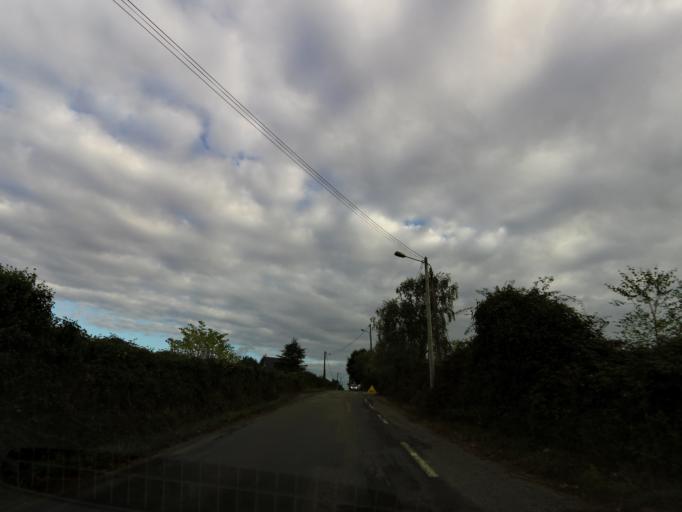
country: FR
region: Brittany
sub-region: Departement d'Ille-et-Vilaine
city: Crevin
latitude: 47.9369
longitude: -1.6545
